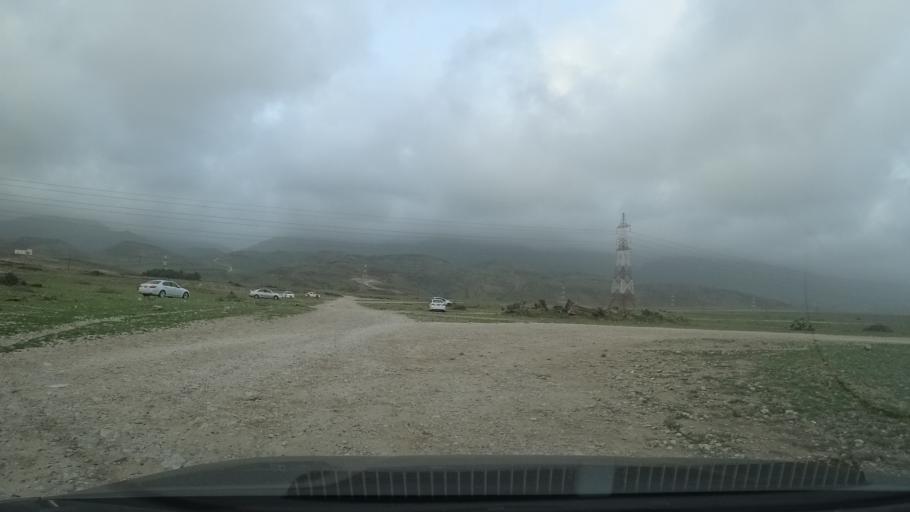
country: OM
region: Zufar
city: Salalah
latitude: 17.1020
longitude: 54.2341
